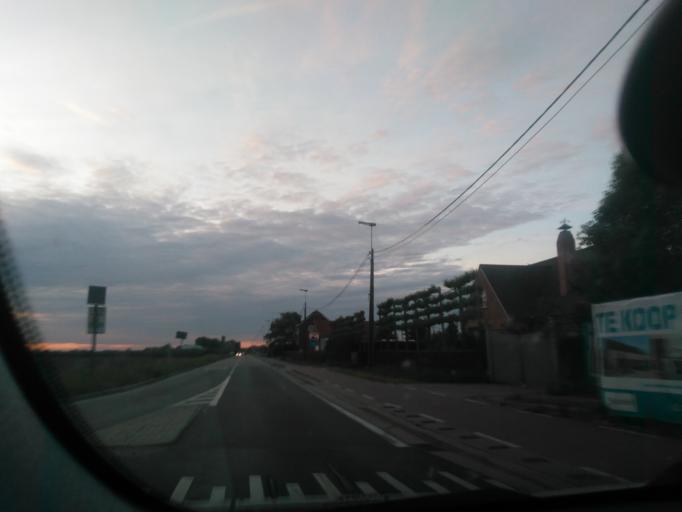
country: BE
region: Flanders
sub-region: Provincie Oost-Vlaanderen
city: Sint-Gillis-Waas
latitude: 51.2616
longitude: 4.1879
